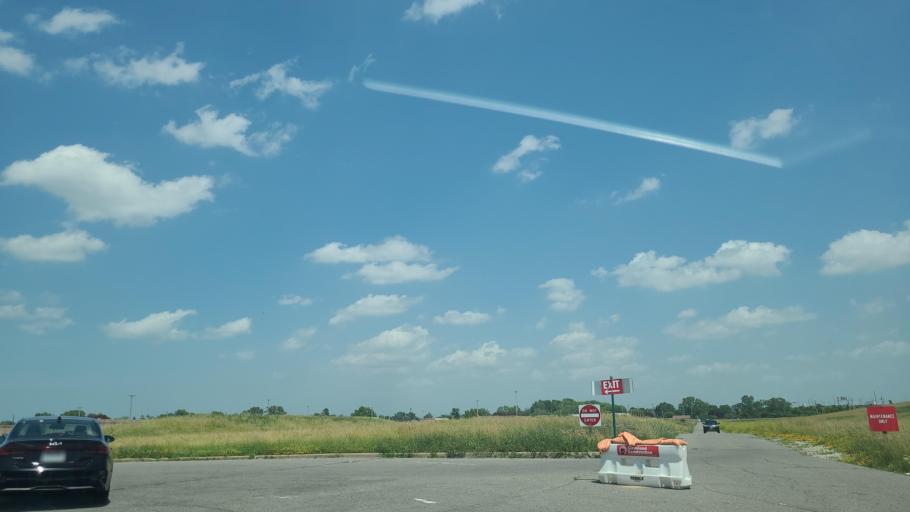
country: US
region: Ohio
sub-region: Cuyahoga County
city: Fairview Park
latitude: 41.4219
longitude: -81.8359
